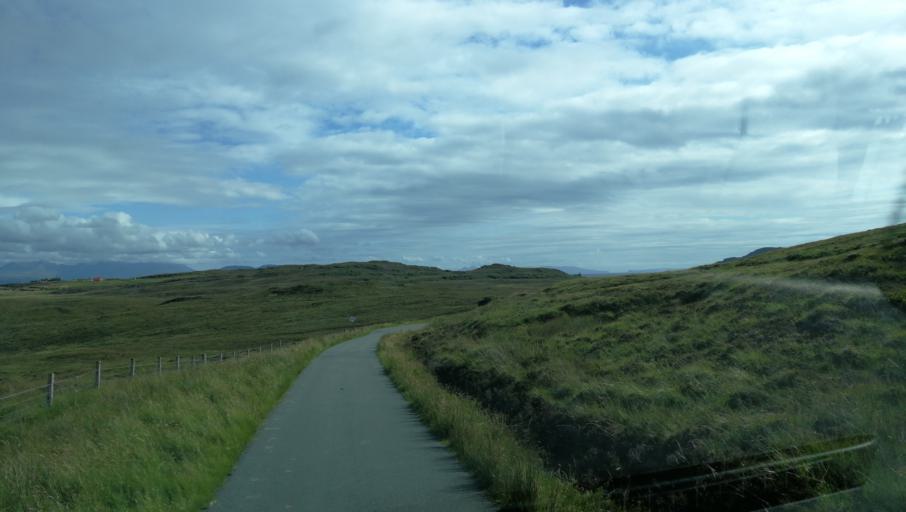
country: GB
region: Scotland
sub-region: Highland
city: Isle of Skye
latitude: 57.4113
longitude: -6.5657
